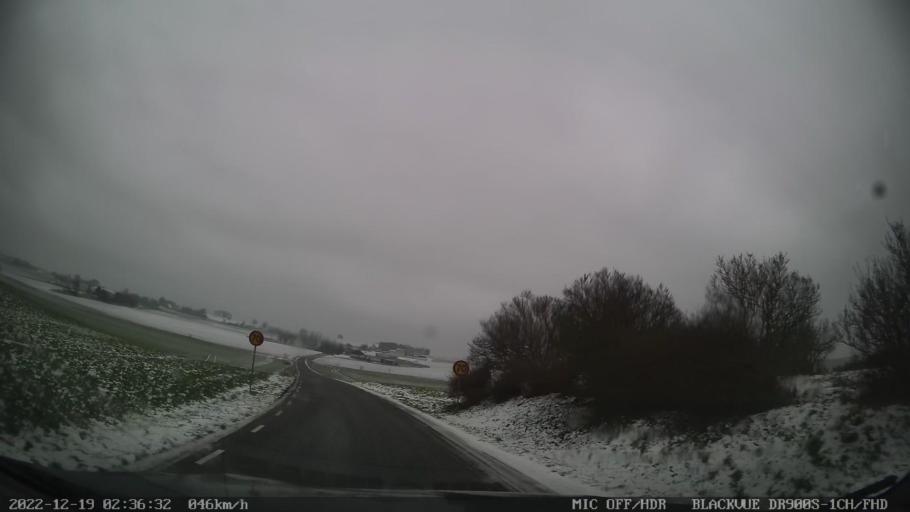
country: SE
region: Skane
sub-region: Tomelilla Kommun
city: Tomelilla
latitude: 55.5257
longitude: 14.0415
